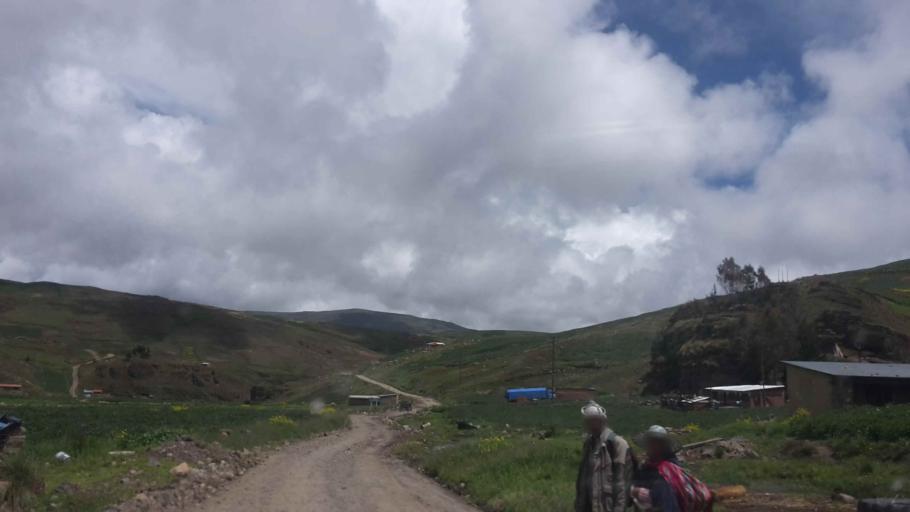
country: BO
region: Cochabamba
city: Cochabamba
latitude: -17.2097
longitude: -66.0852
